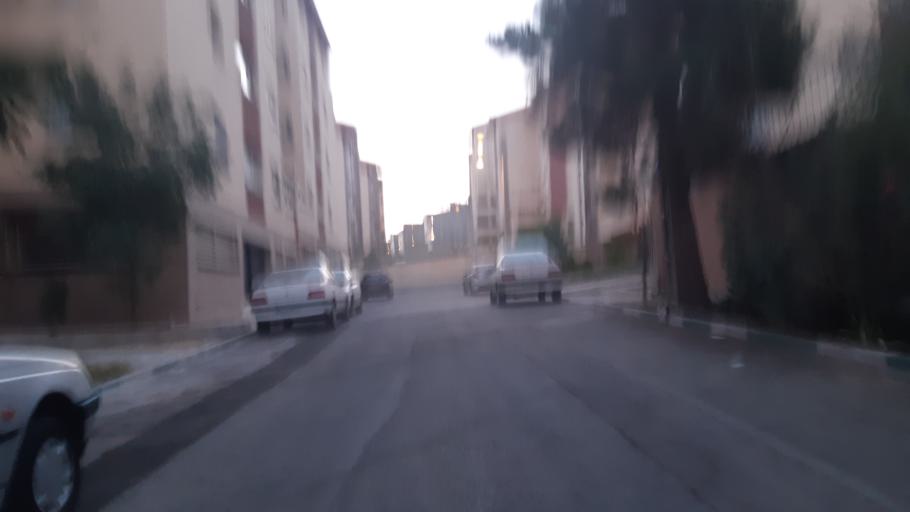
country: IR
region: Tehran
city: Shahr-e Qods
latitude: 35.7553
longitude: 51.1522
